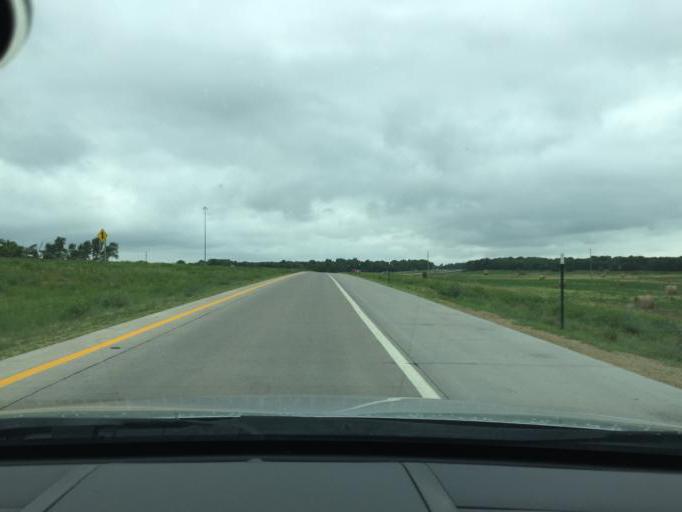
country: US
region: Kansas
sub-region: Reno County
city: Buhler
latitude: 38.1537
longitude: -97.8496
